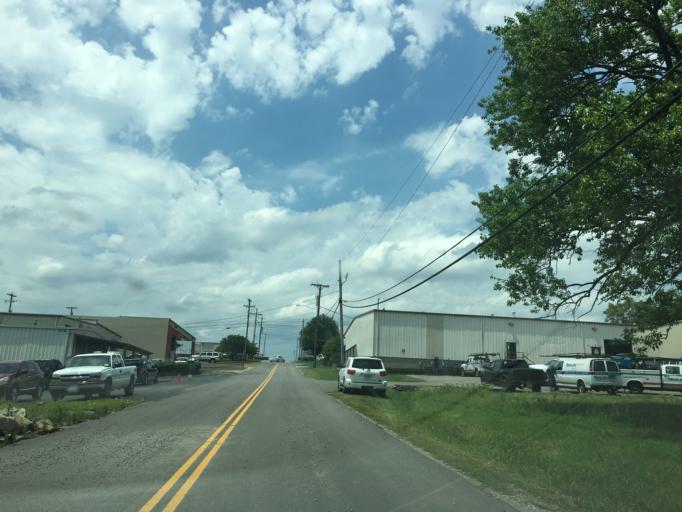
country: US
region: Tennessee
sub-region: Davidson County
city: Oak Hill
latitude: 36.1189
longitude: -86.7519
